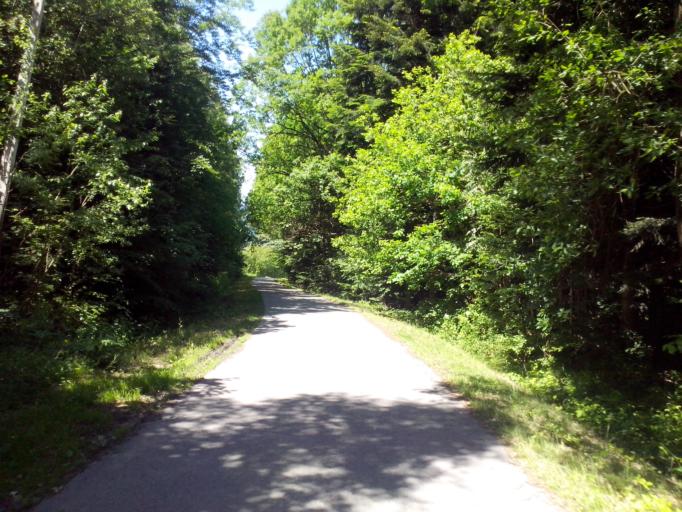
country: PL
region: Subcarpathian Voivodeship
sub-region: Powiat strzyzowski
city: Wysoka Strzyzowska
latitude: 49.8181
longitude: 21.7677
